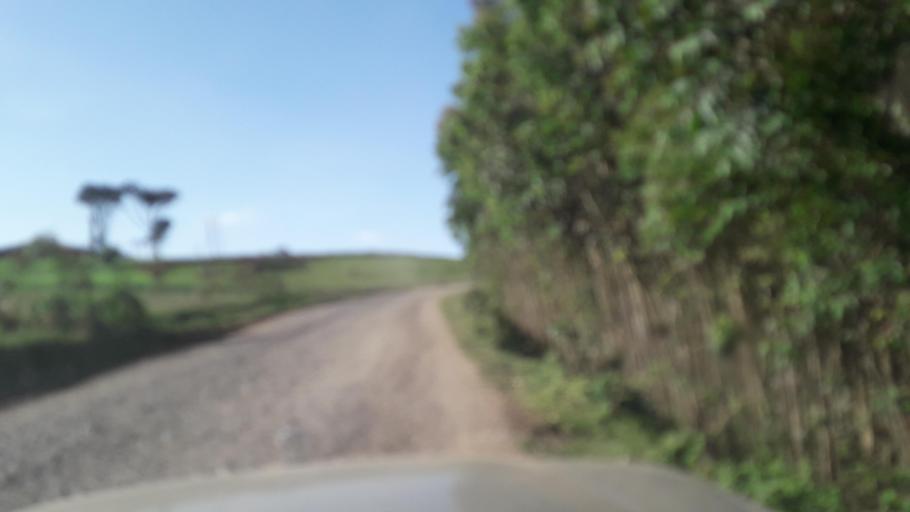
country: ET
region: Oromiya
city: Jima
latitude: 7.4458
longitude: 36.8798
